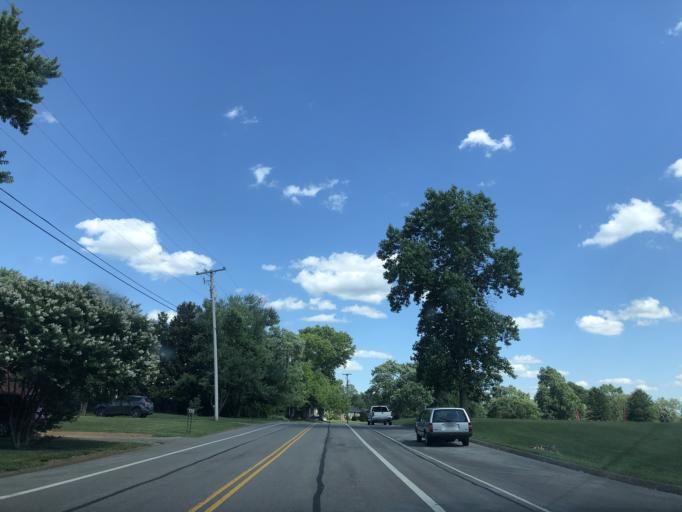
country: US
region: Tennessee
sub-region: Davidson County
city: Belle Meade
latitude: 36.0606
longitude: -86.9381
